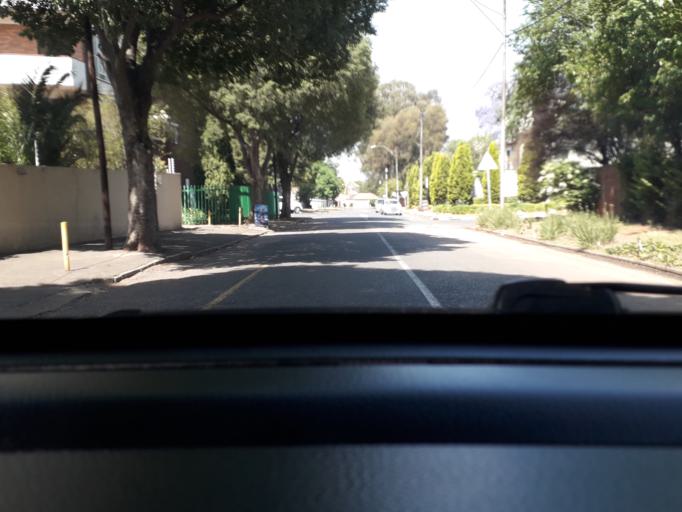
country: ZA
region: Gauteng
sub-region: City of Johannesburg Metropolitan Municipality
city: Johannesburg
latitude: -26.1362
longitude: 28.0518
